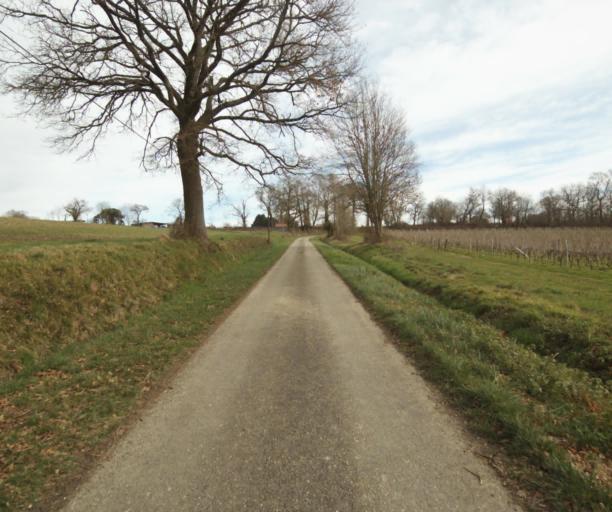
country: FR
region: Aquitaine
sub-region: Departement des Landes
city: Gabarret
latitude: 43.9587
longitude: 0.0112
